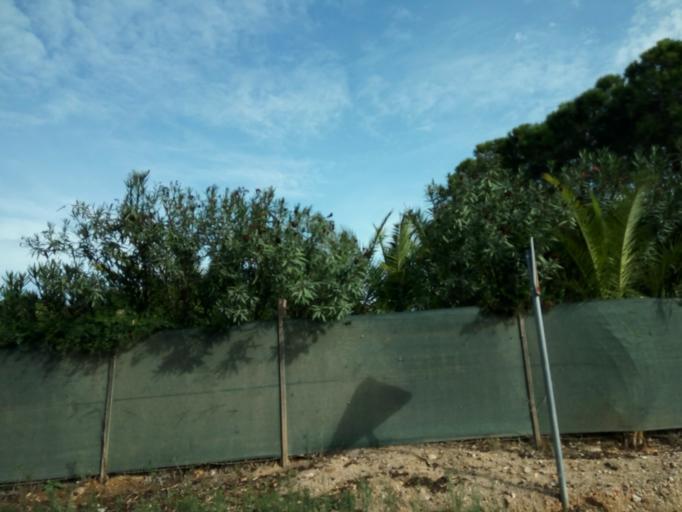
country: PT
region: Faro
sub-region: Faro
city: Faro
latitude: 37.0294
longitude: -7.9750
